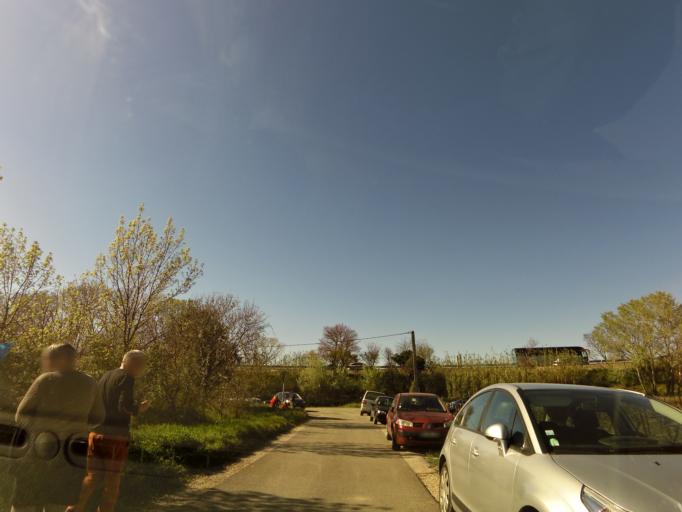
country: FR
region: Languedoc-Roussillon
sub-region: Departement de l'Herault
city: Villetelle
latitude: 43.7213
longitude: 4.1474
